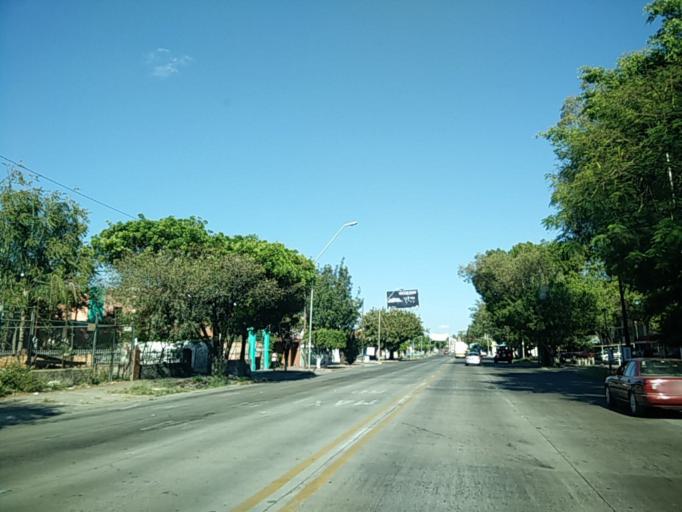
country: MX
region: Jalisco
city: Tlaquepaque
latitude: 20.6587
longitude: -103.3298
